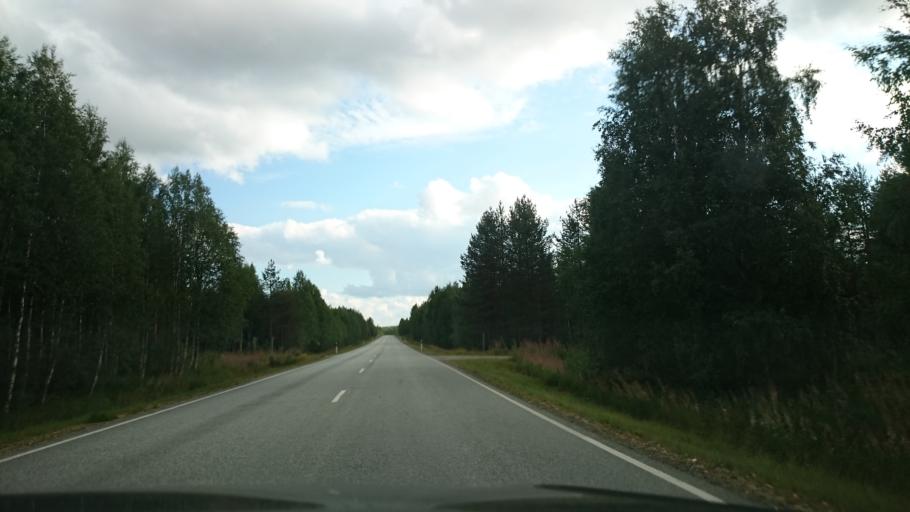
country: FI
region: Kainuu
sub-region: Kehys-Kainuu
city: Kuhmo
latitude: 64.5274
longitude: 29.9451
